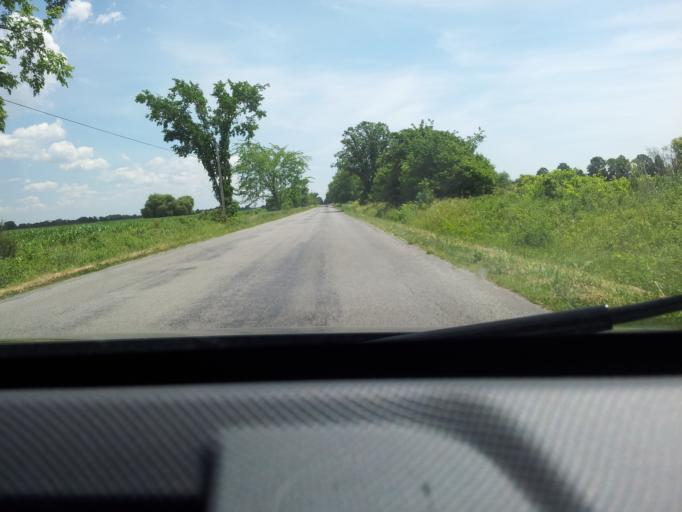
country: CA
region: Ontario
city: Norfolk County
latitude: 42.8264
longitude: -80.2689
